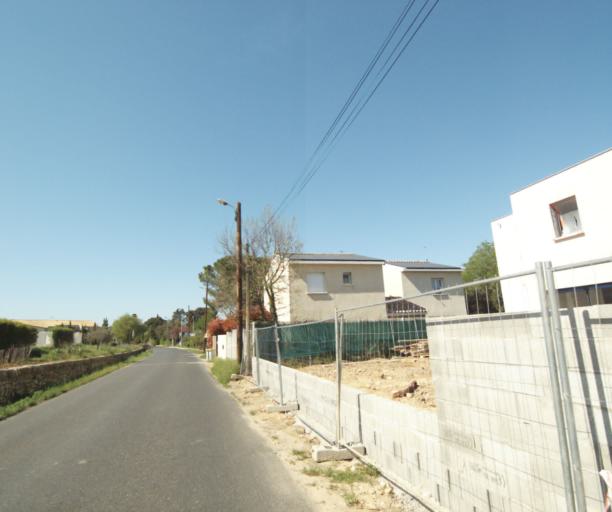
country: FR
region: Languedoc-Roussillon
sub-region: Departement de l'Herault
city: Castries
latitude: 43.6819
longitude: 3.9845
